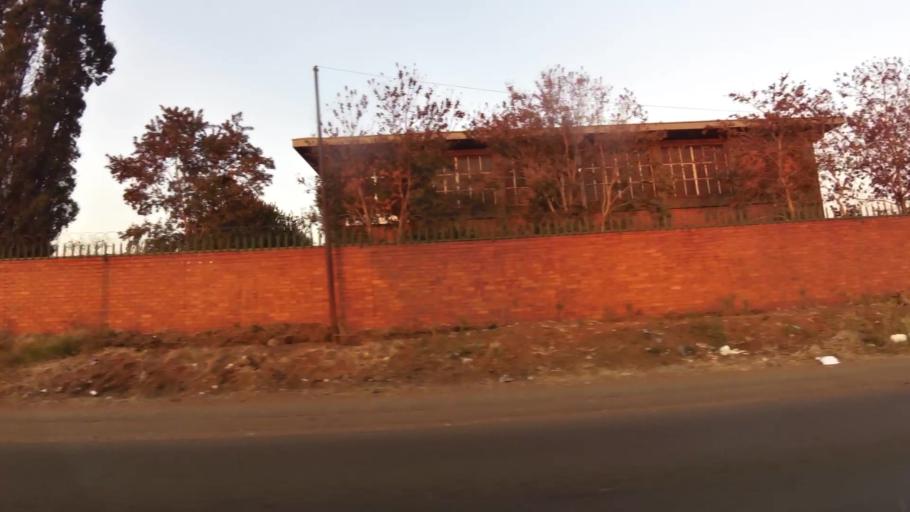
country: ZA
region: Gauteng
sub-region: City of Johannesburg Metropolitan Municipality
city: Soweto
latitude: -26.2873
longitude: 27.8911
